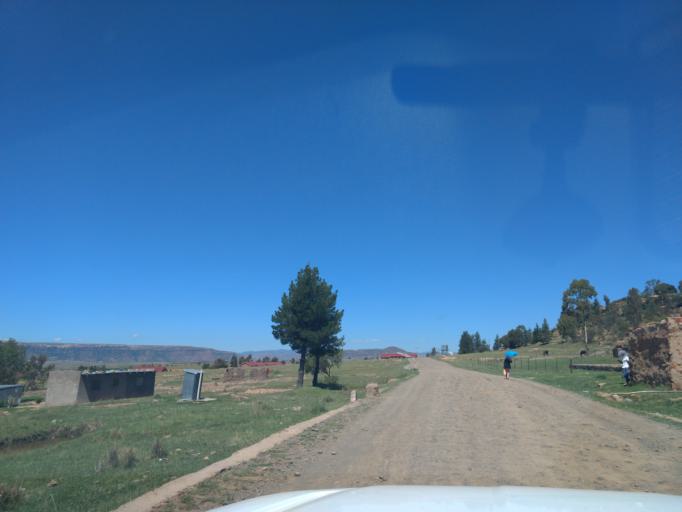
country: LS
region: Maseru
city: Maseru
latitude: -29.4937
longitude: 27.3722
